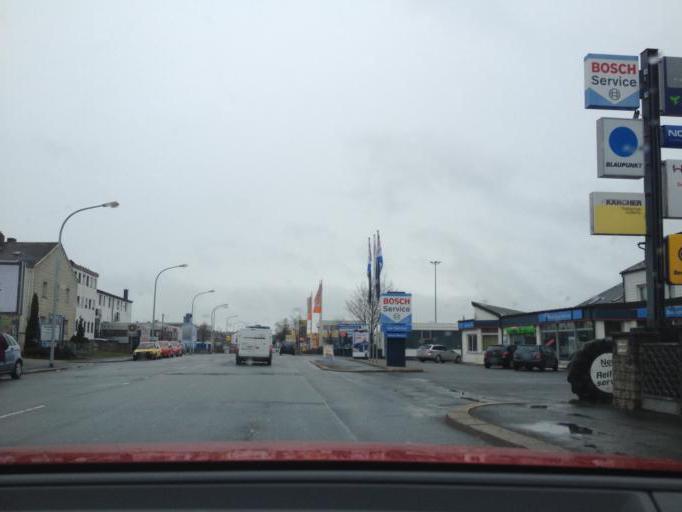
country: DE
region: Bavaria
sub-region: Upper Franconia
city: Hof
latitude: 50.3038
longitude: 11.9221
